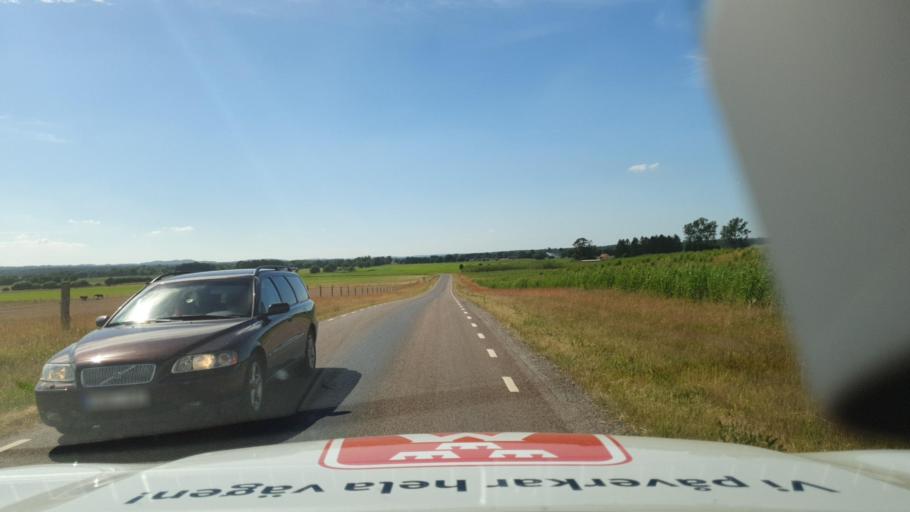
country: SE
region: Skane
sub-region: Sjobo Kommun
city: Sjoebo
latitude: 55.6191
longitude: 13.6508
